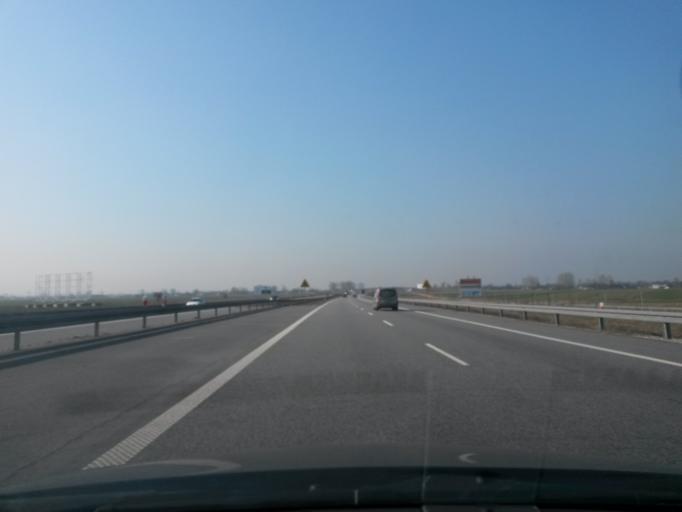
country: PL
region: Lodz Voivodeship
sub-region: powiat Lowicki
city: Lyszkowice
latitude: 52.0076
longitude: 19.9539
